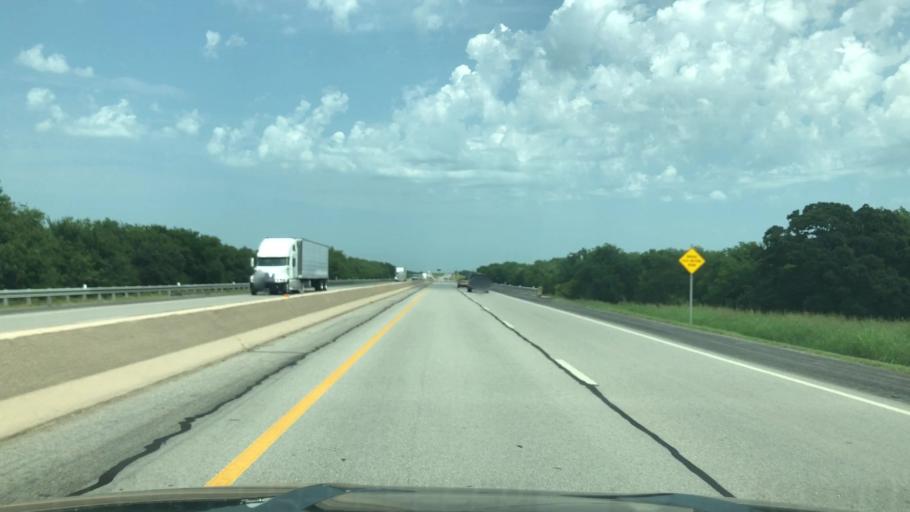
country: US
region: Oklahoma
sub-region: Rogers County
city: Catoosa
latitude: 36.1947
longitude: -95.7185
